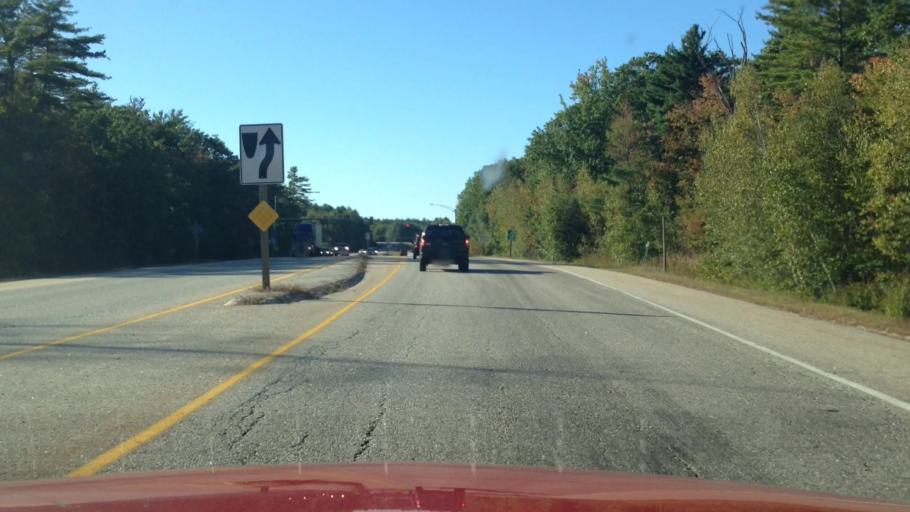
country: US
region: Maine
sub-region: Cumberland County
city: South Portland Gardens
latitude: 43.6696
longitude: -70.3352
